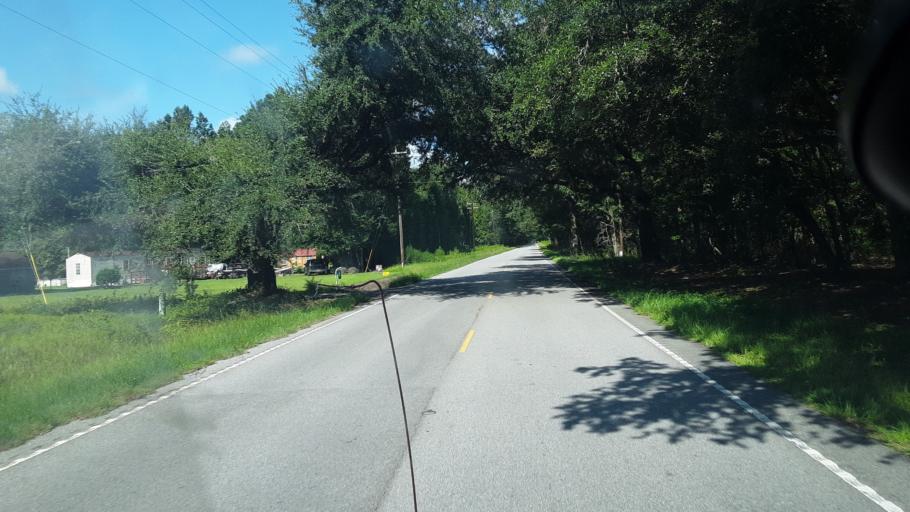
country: US
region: South Carolina
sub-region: Jasper County
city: Ridgeland
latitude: 32.5901
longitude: -80.9640
